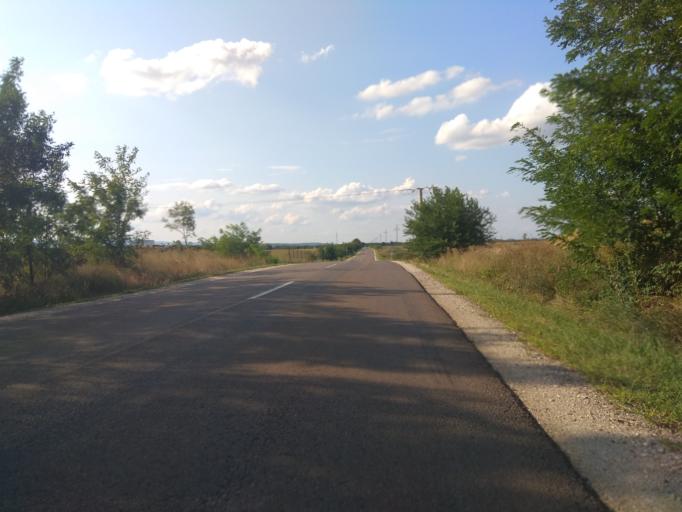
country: HU
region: Borsod-Abauj-Zemplen
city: Emod
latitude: 47.9168
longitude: 20.8820
